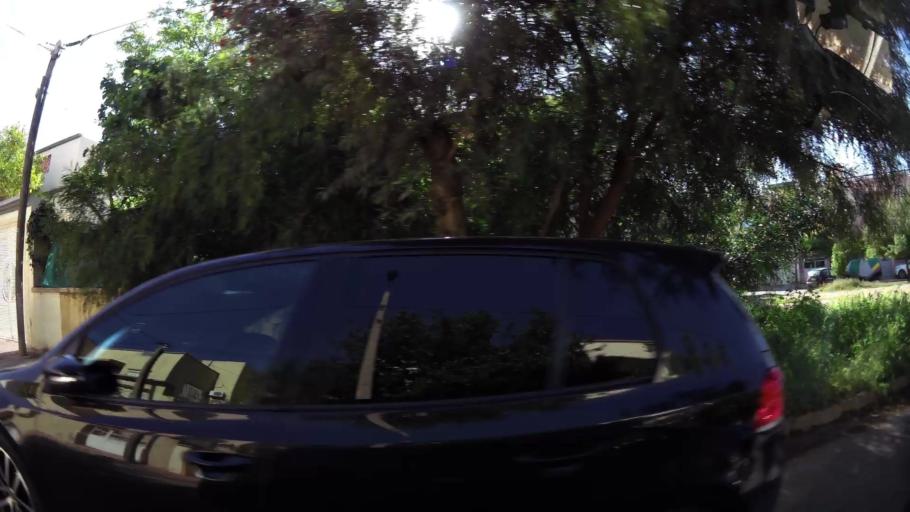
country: MA
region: Oriental
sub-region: Oujda-Angad
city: Oujda
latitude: 34.6657
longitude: -1.9086
